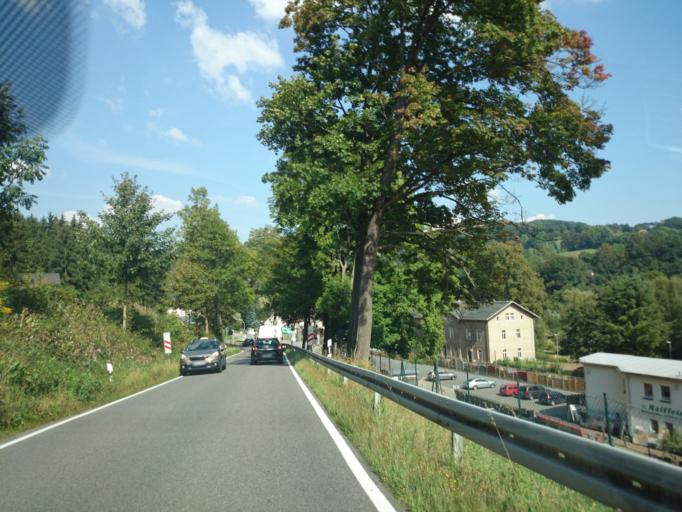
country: DE
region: Saxony
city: Zschopau
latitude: 50.7623
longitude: 13.0896
